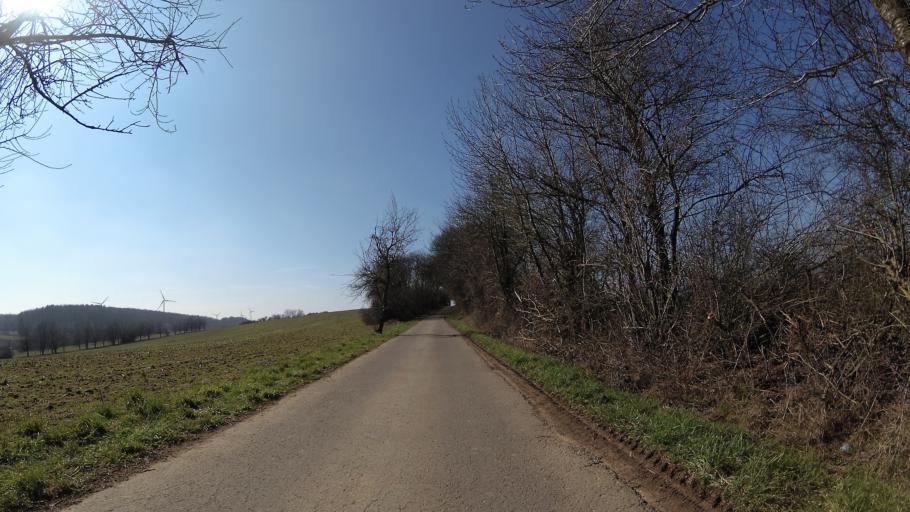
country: DE
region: Saarland
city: Eppelborn
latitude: 49.4385
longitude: 7.0030
